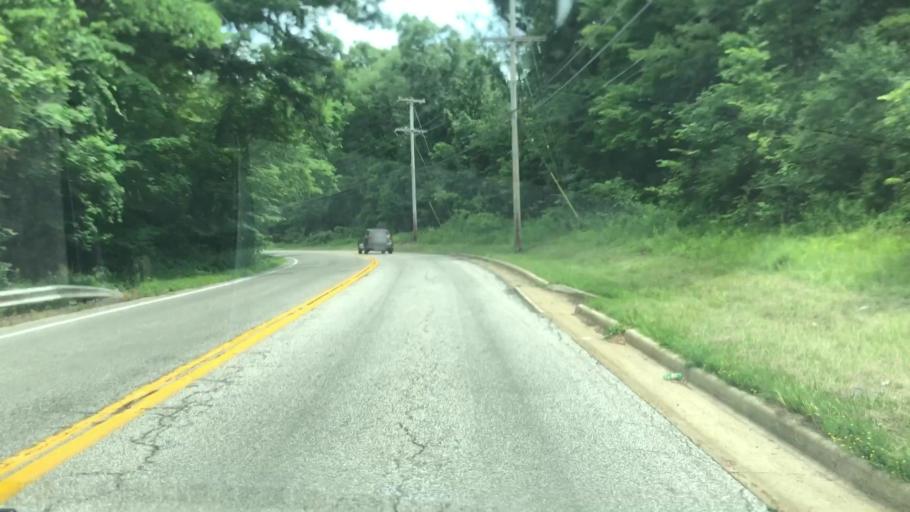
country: US
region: Ohio
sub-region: Summit County
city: Fairlawn
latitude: 41.1696
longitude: -81.5644
